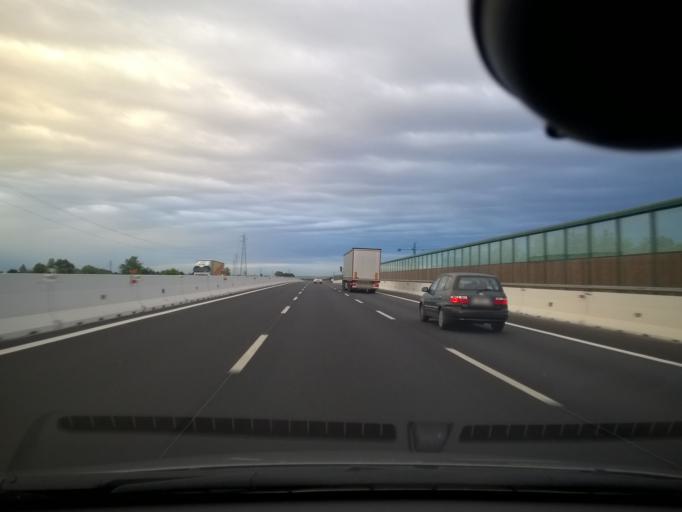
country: IT
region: Veneto
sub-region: Provincia di Treviso
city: Musestre
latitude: 45.5910
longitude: 12.3715
